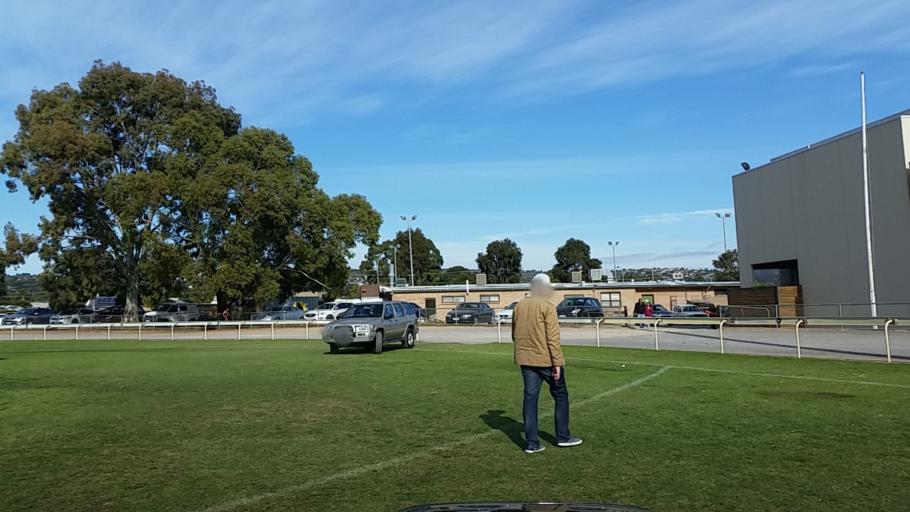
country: AU
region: South Australia
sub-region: Marion
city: Sturt
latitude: -35.0161
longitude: 138.5532
